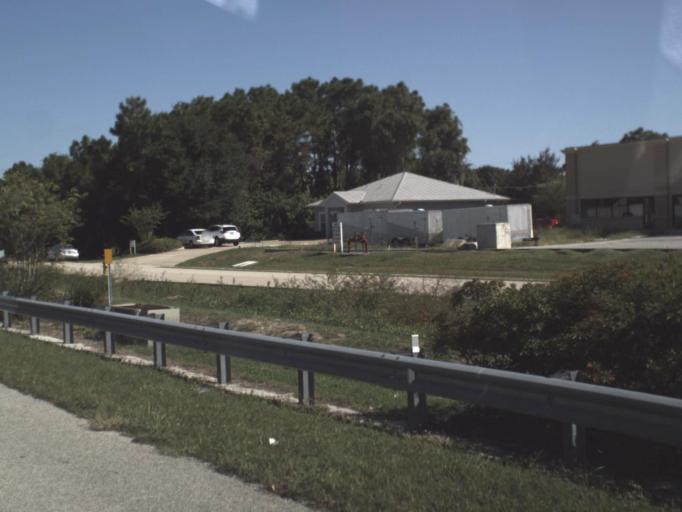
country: US
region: Florida
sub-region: Charlotte County
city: Grove City
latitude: 26.9343
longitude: -82.2945
